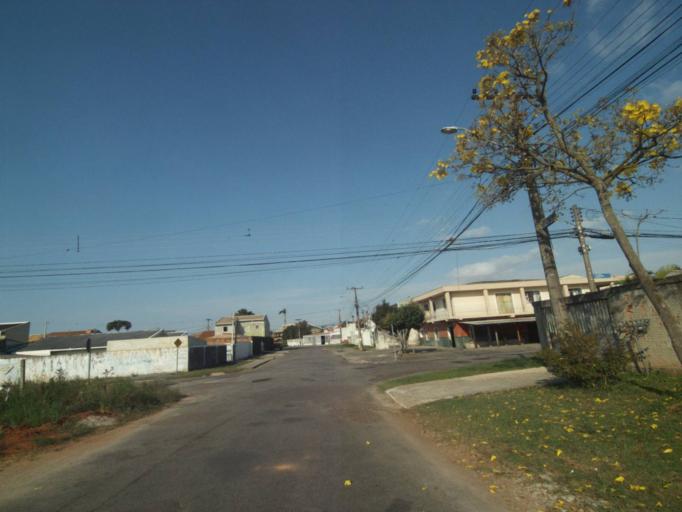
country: BR
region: Parana
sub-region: Curitiba
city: Curitiba
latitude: -25.4828
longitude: -49.3341
